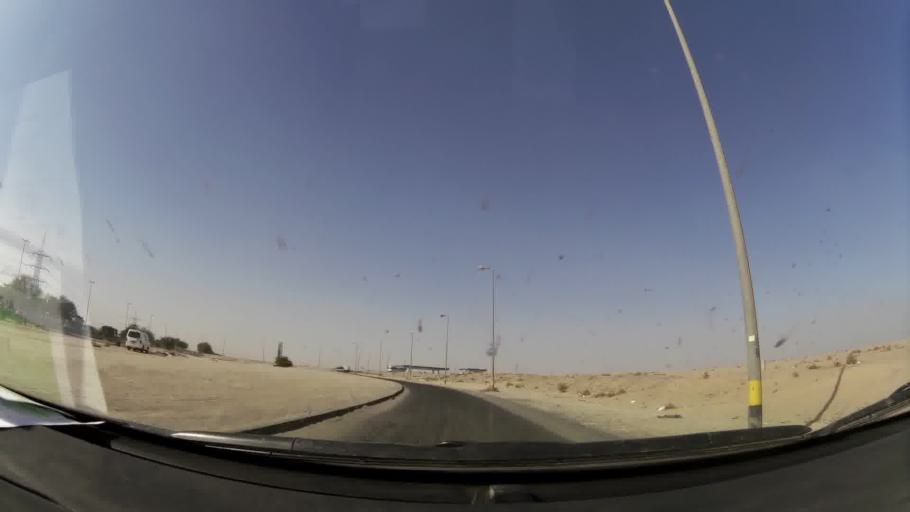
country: KW
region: Al Asimah
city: Ar Rabiyah
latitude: 29.2744
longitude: 47.8120
